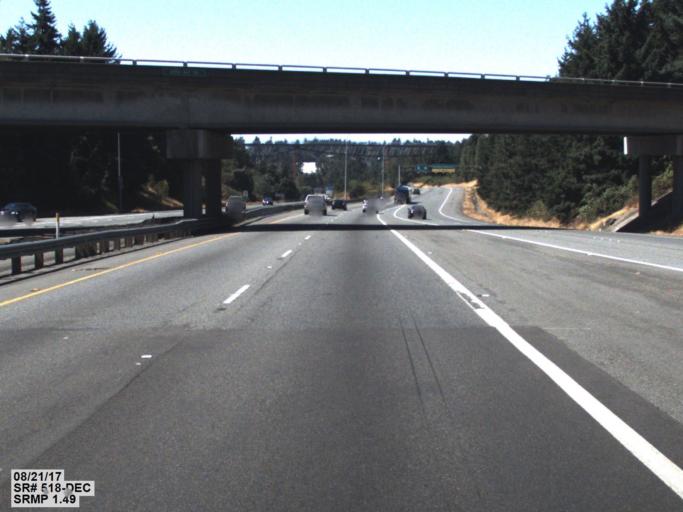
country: US
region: Washington
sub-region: King County
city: Riverton
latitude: 47.4662
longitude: -122.3017
